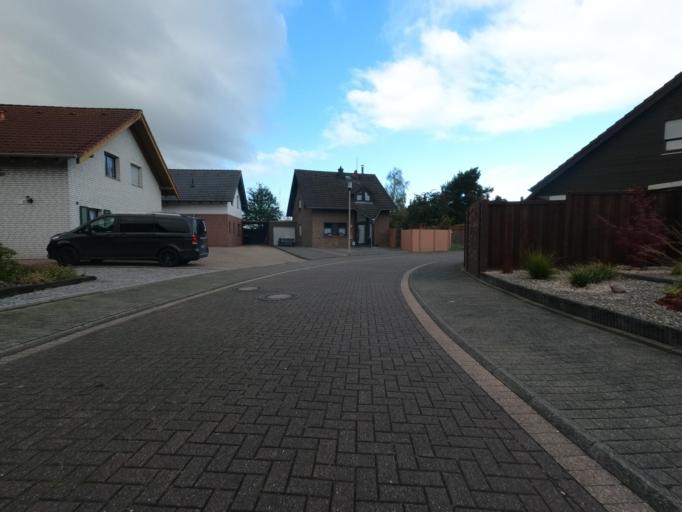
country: DE
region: North Rhine-Westphalia
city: Huckelhoven
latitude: 51.0614
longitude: 6.2081
